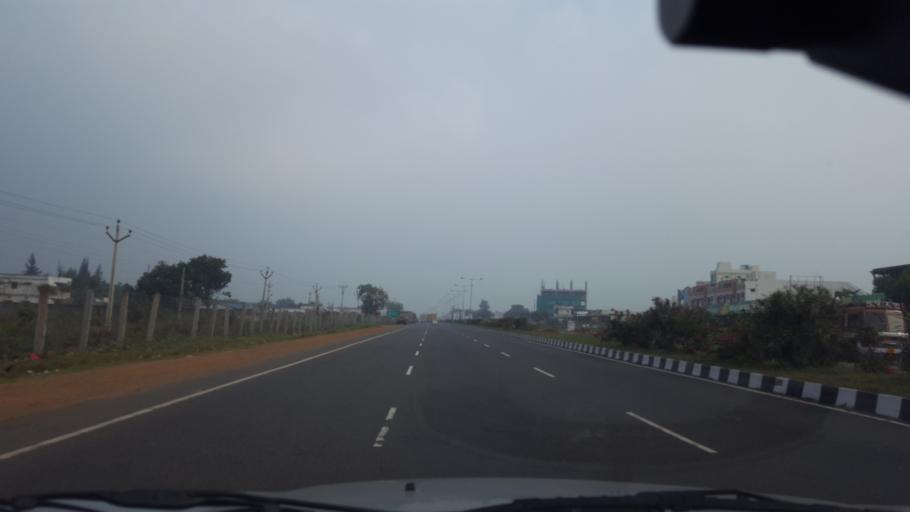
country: IN
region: Andhra Pradesh
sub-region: Prakasam
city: Addanki
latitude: 15.6820
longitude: 80.0176
